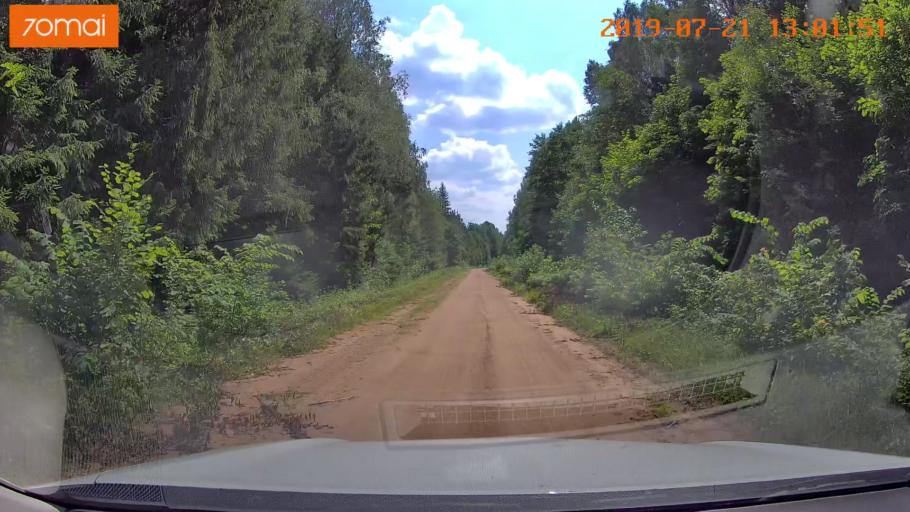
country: BY
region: Grodnenskaya
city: Lyubcha
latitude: 53.8506
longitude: 26.0224
